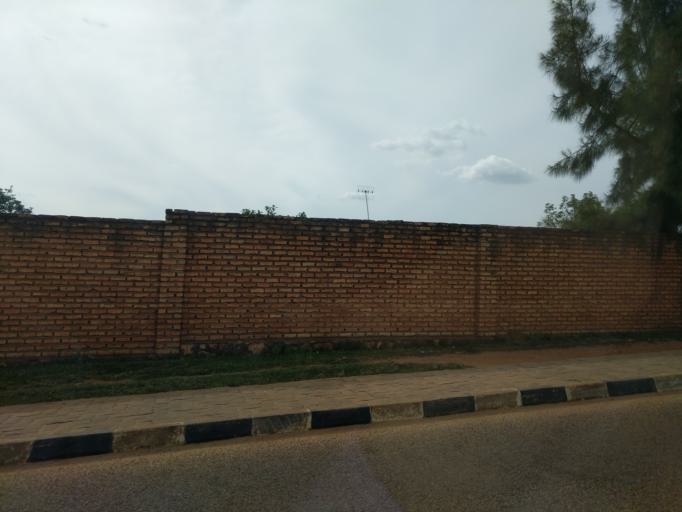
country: RW
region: Kigali
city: Kigali
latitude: -1.9796
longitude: 30.1336
